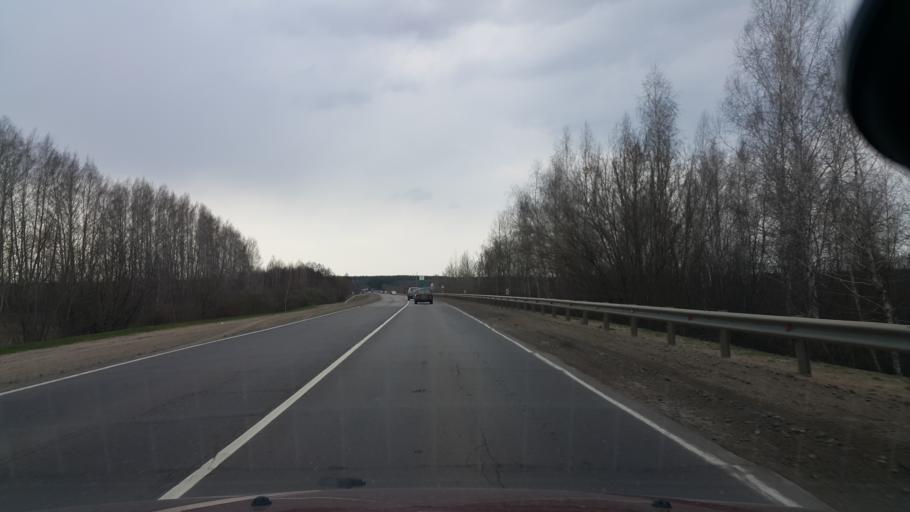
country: RU
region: Tambov
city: Znamenka
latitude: 52.5191
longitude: 41.3639
